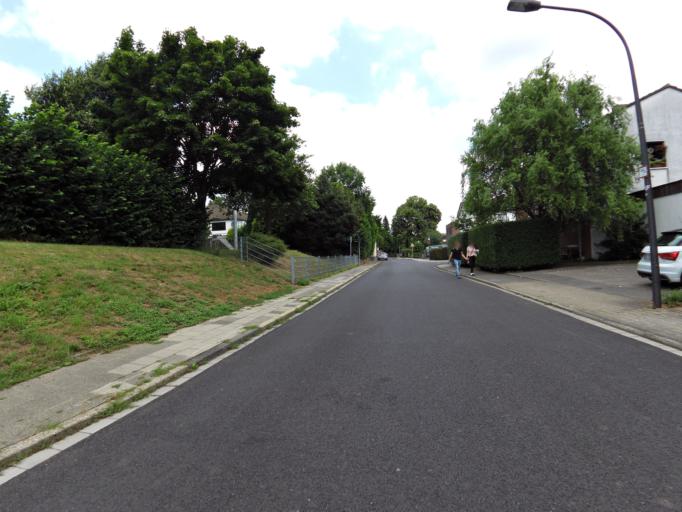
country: NL
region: Limburg
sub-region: Gemeente Kerkrade
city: Kerkrade
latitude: 50.8363
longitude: 6.0479
